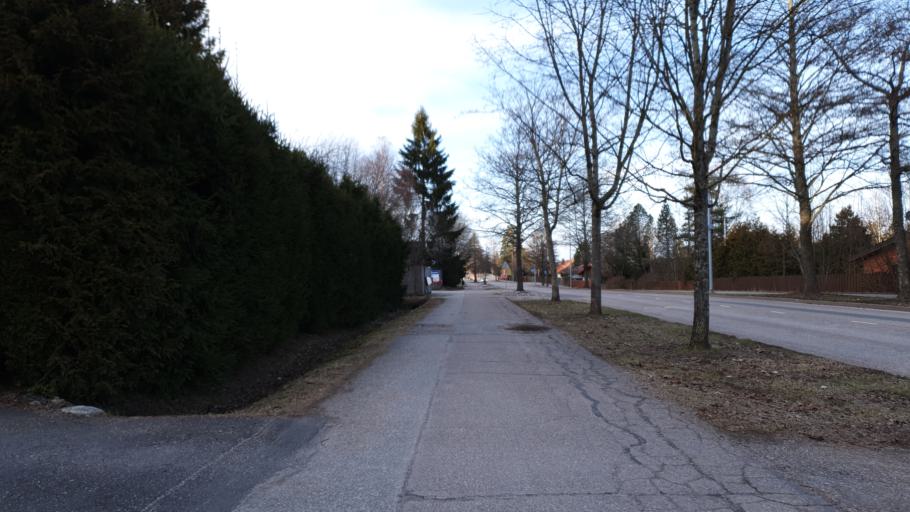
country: FI
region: Uusimaa
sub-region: Helsinki
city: Vantaa
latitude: 60.3167
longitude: 25.0137
